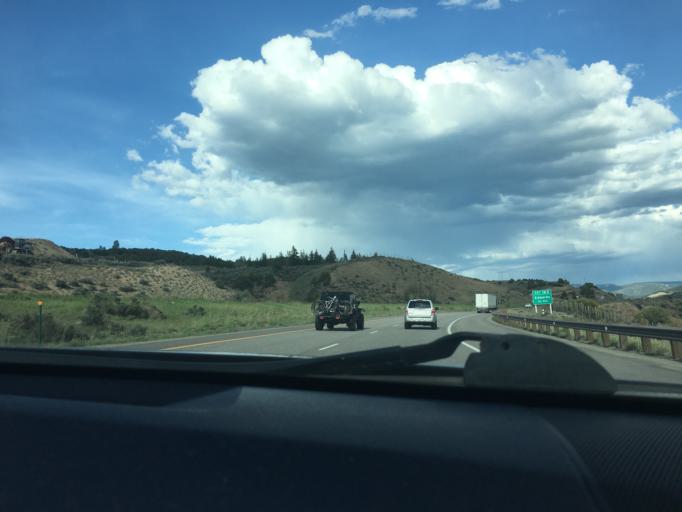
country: US
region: Colorado
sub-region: Eagle County
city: Edwards
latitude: 39.6546
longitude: -106.6044
